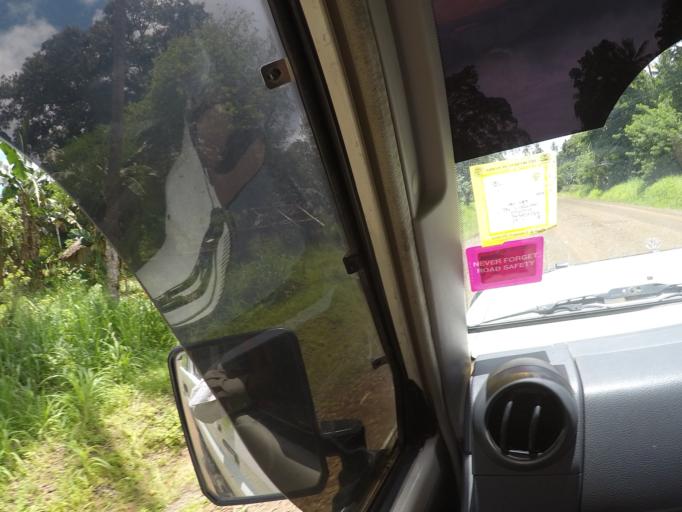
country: PG
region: Milne Bay
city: Alotau
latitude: -10.3413
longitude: 150.6272
